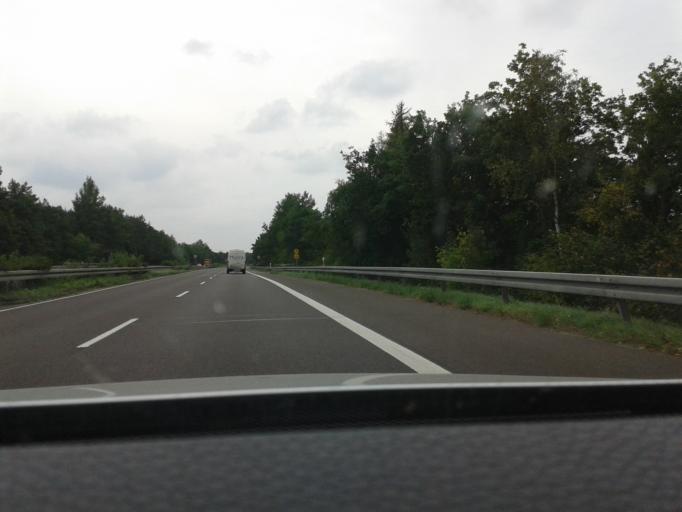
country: DE
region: Lower Saxony
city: Burgdorf
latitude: 52.4514
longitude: 9.9434
